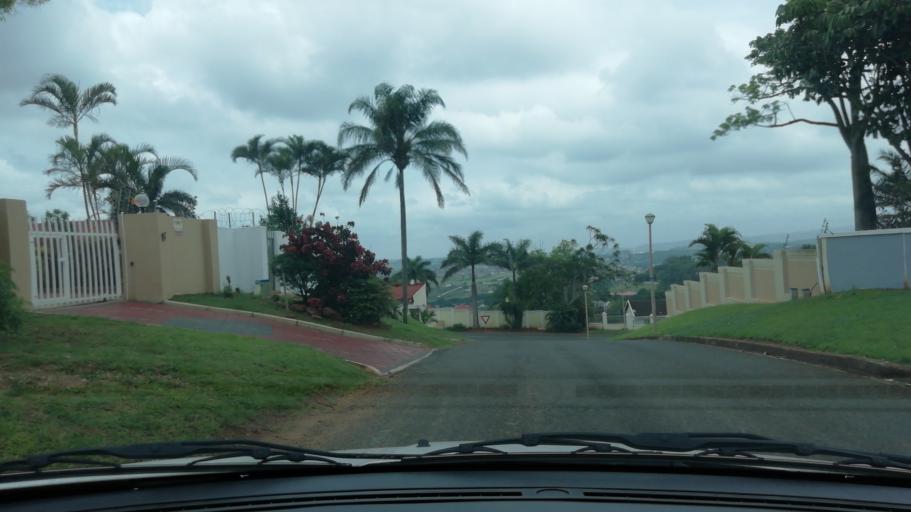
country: ZA
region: KwaZulu-Natal
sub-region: uThungulu District Municipality
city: Empangeni
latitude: -28.7552
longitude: 31.8869
